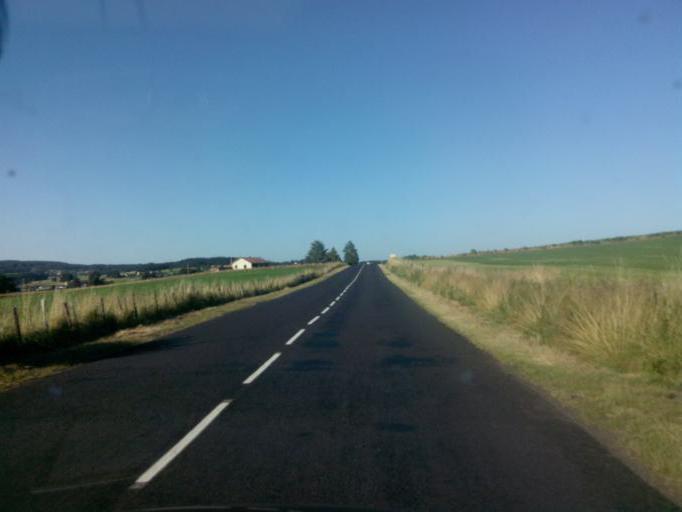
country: FR
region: Auvergne
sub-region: Departement de la Haute-Loire
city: Craponne-sur-Arzon
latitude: 45.3257
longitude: 3.8301
